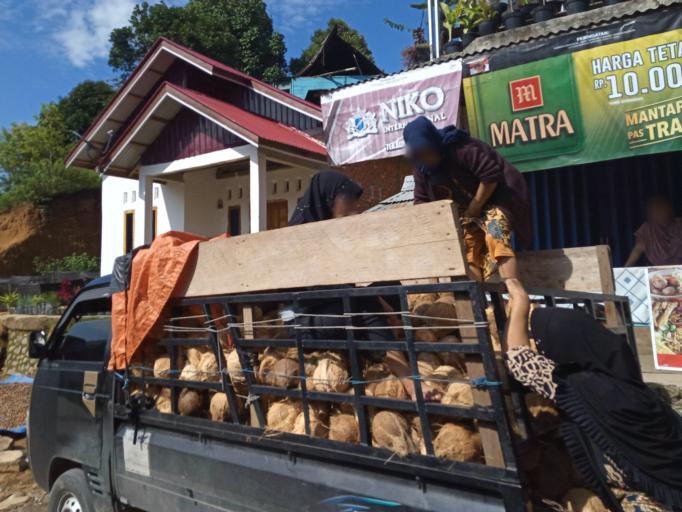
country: ID
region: Jambi
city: Sungai Penuh
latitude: -2.1636
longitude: 101.5909
